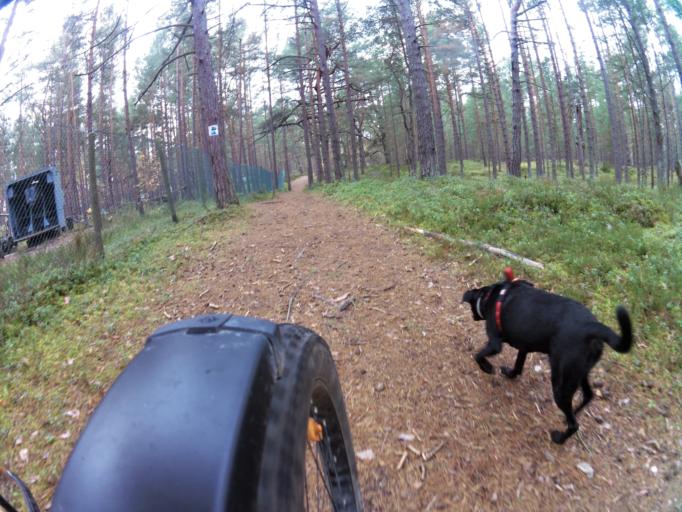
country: PL
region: Pomeranian Voivodeship
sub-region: Powiat pucki
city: Hel
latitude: 54.6239
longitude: 18.8017
